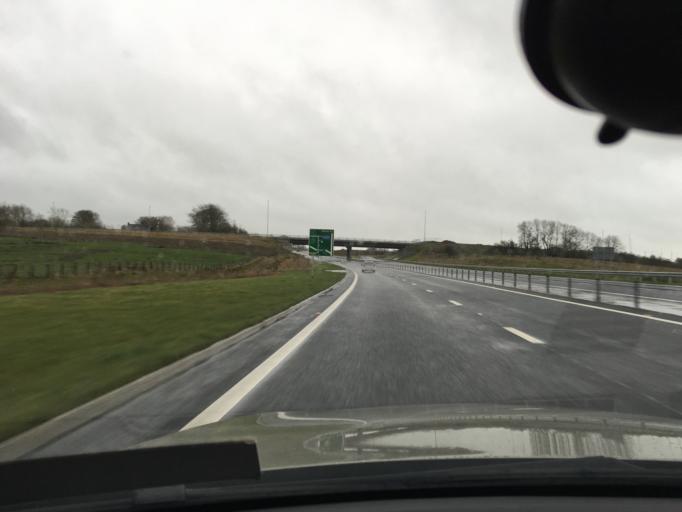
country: GB
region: Northern Ireland
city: Ballyclare
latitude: 54.7702
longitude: -5.9634
